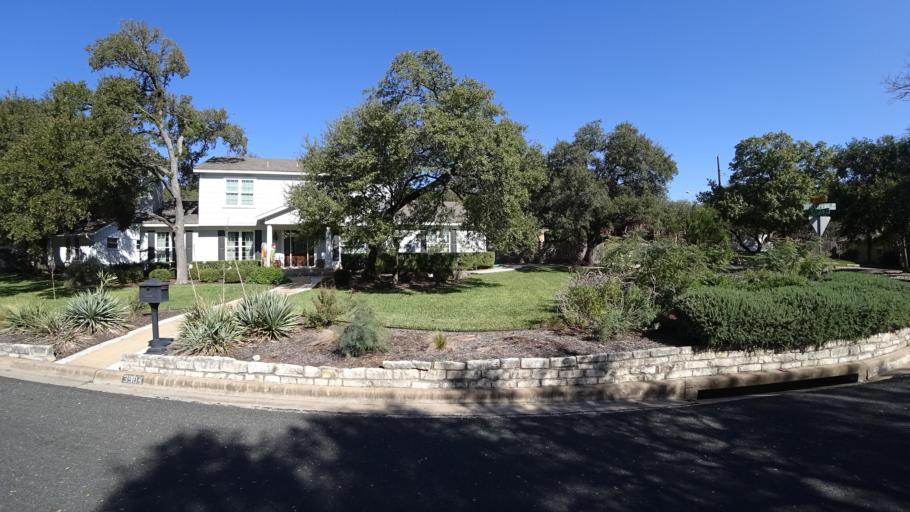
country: US
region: Texas
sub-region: Williamson County
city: Jollyville
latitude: 30.3799
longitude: -97.7452
